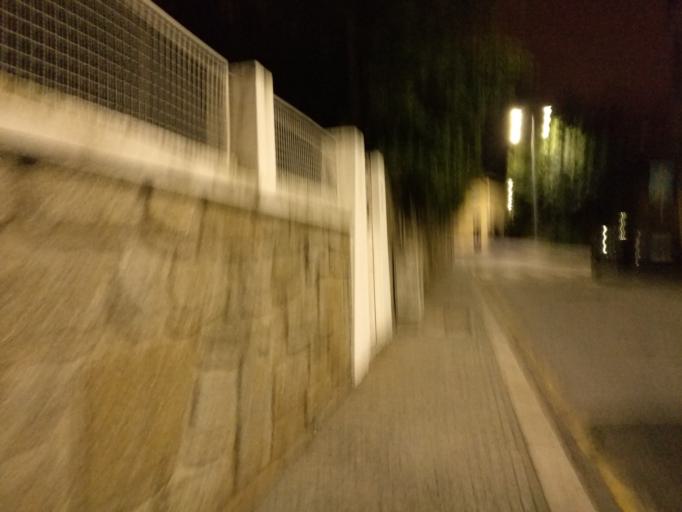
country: PT
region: Porto
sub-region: Vila Nova de Gaia
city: Vilar de Andorinho
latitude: 41.1067
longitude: -8.6019
